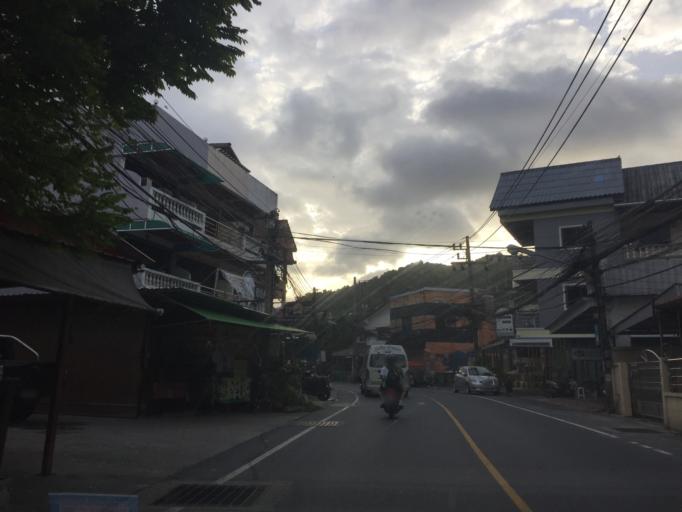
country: TH
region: Phuket
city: Patong
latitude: 7.8962
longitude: 98.3080
